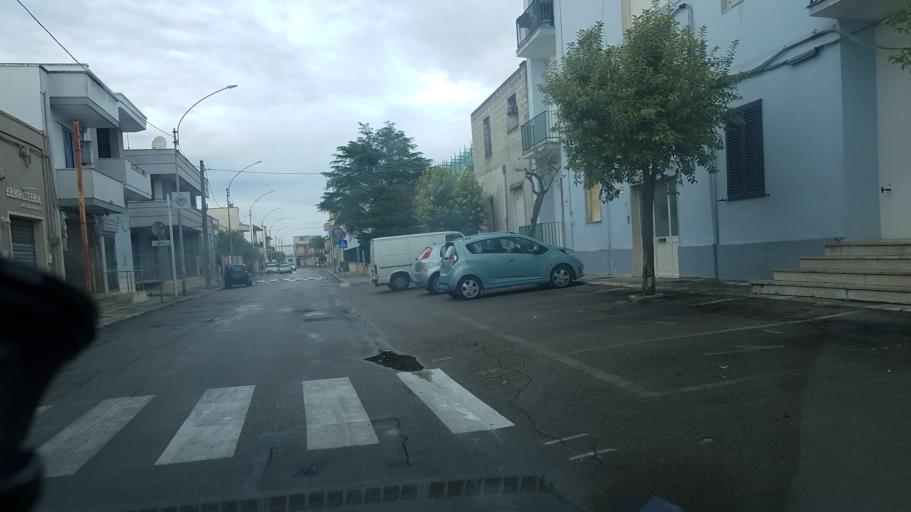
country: IT
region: Apulia
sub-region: Provincia di Lecce
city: Salice Salentino
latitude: 40.3857
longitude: 17.9602
